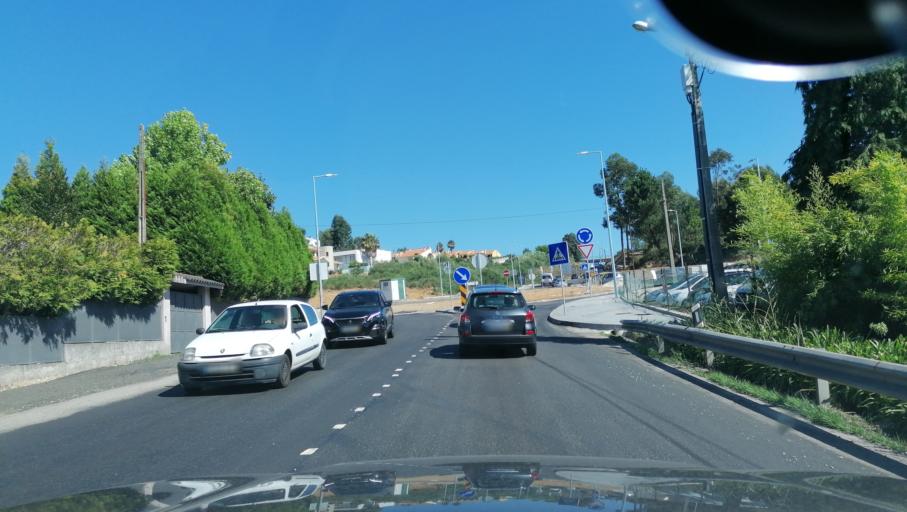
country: PT
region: Aveiro
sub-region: Santa Maria da Feira
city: Arrifana
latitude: 40.9297
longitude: -8.5122
